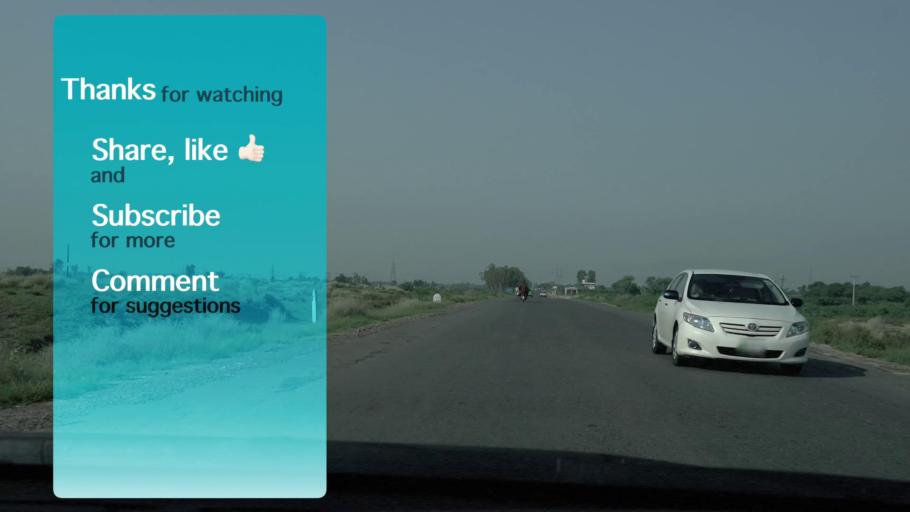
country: PK
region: Punjab
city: Gojra
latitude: 31.1112
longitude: 72.6620
